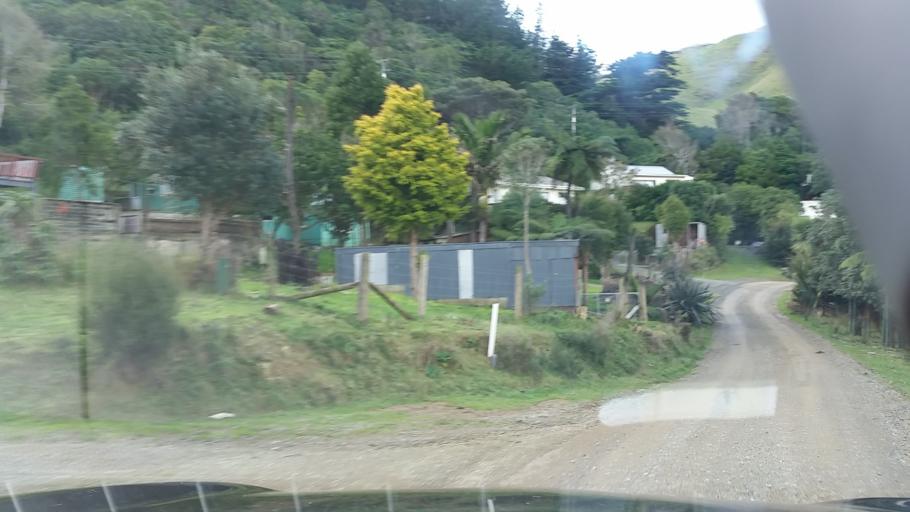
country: NZ
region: Marlborough
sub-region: Marlborough District
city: Picton
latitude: -40.9888
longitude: 173.8270
